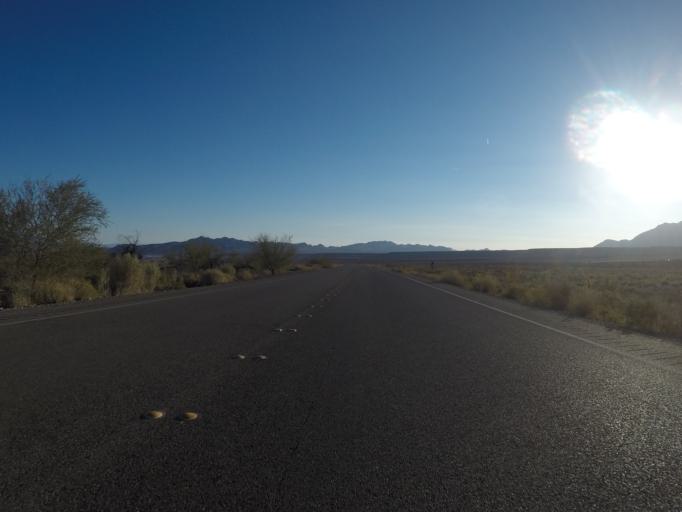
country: US
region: Nevada
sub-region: Clark County
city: Moapa Valley
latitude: 36.3740
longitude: -114.4429
